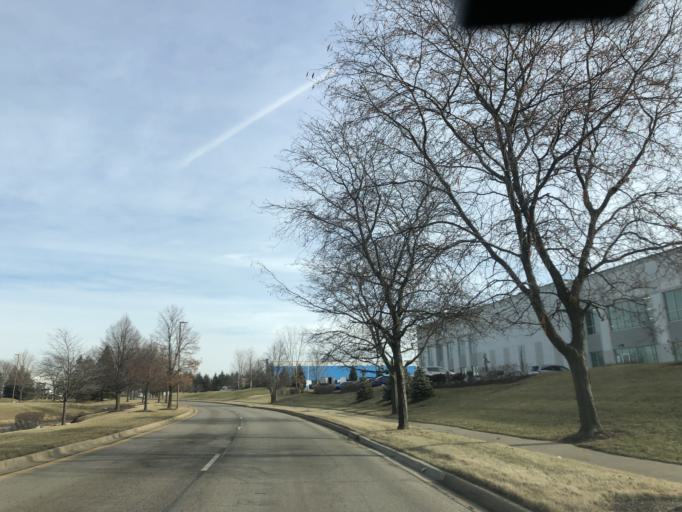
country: US
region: Illinois
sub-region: Cook County
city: Lemont
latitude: 41.6961
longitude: -88.0126
